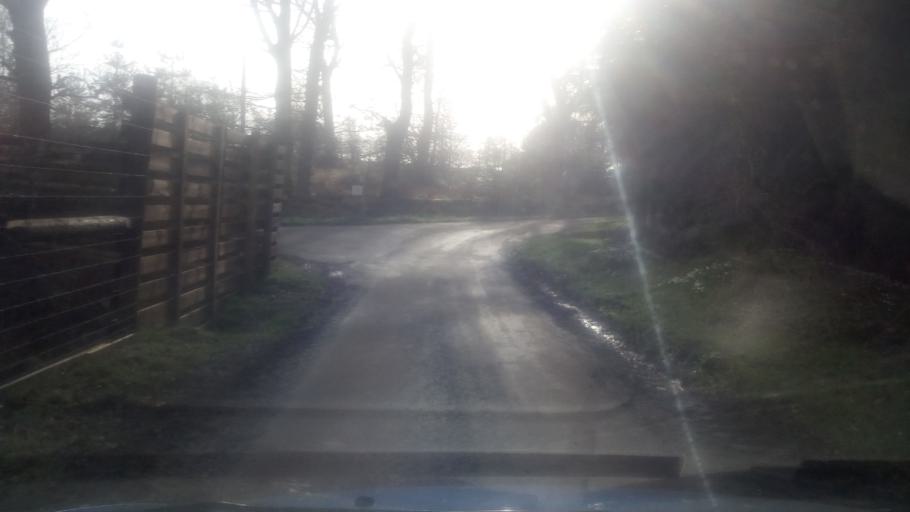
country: GB
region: Scotland
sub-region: The Scottish Borders
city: Jedburgh
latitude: 55.4279
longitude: -2.6406
